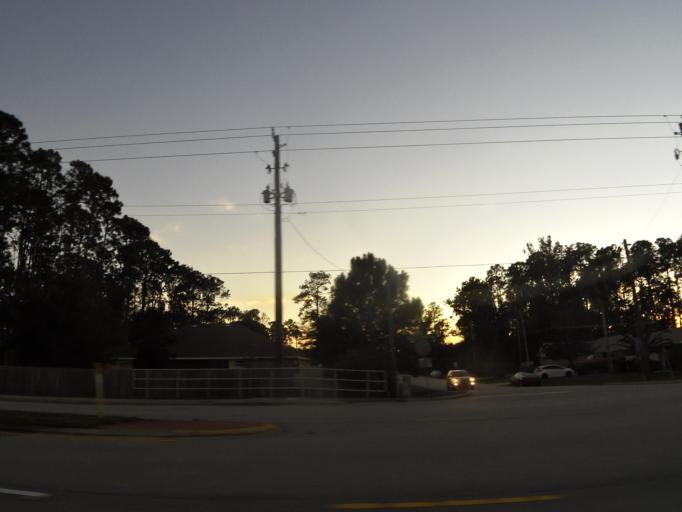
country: US
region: Florida
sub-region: Flagler County
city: Palm Coast
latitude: 29.5651
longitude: -81.2441
